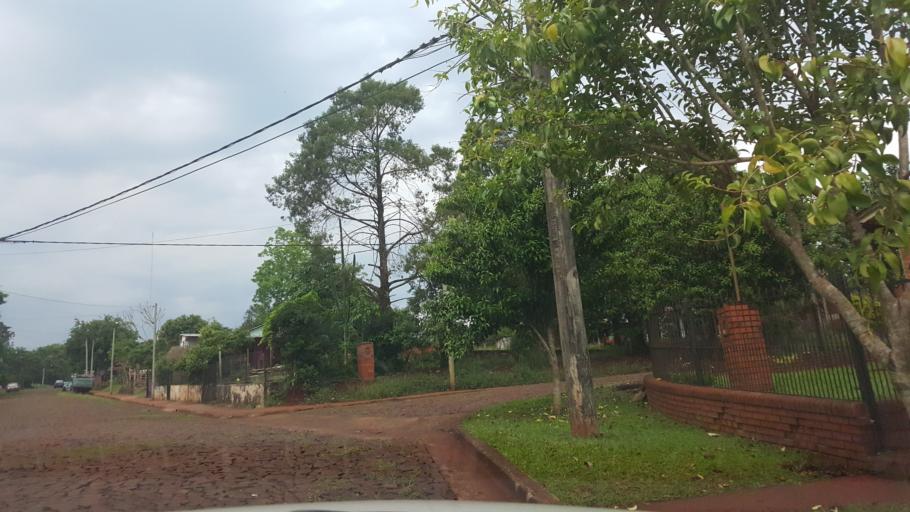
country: AR
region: Misiones
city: Capiovi
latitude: -26.9273
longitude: -55.0627
